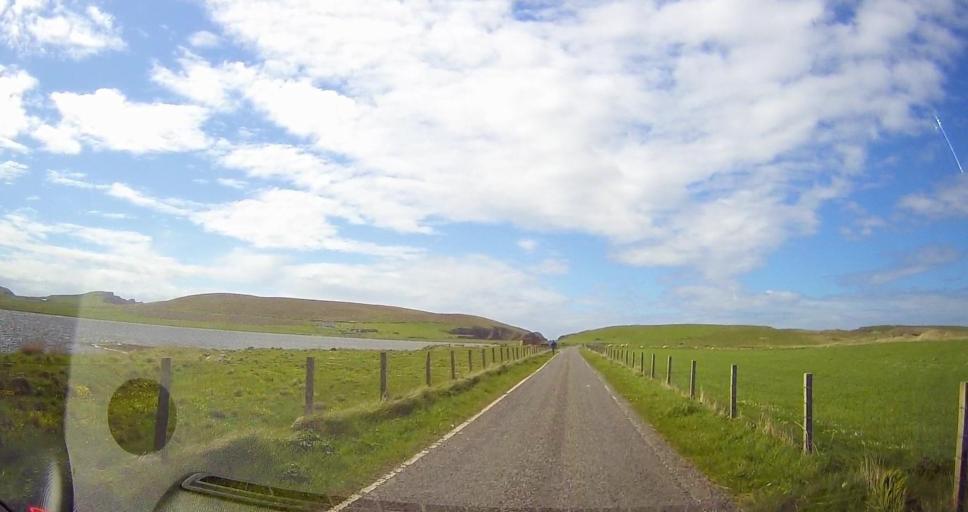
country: GB
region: Scotland
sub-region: Shetland Islands
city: Sandwick
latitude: 59.9417
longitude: -1.3334
